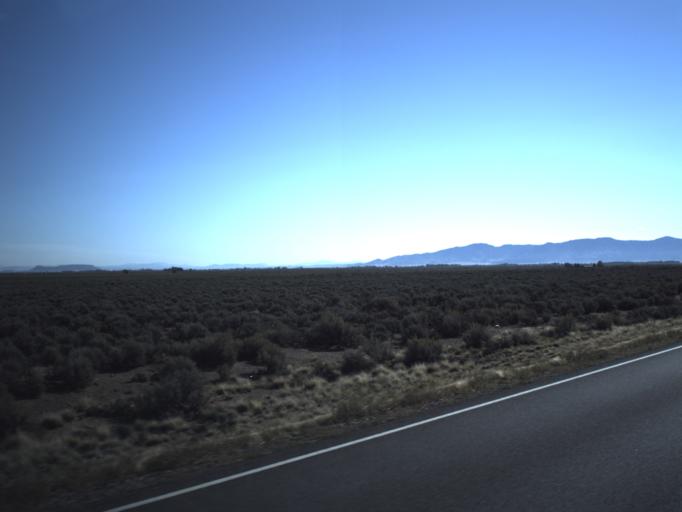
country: US
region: Utah
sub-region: Washington County
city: Enterprise
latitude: 37.7375
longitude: -113.7343
